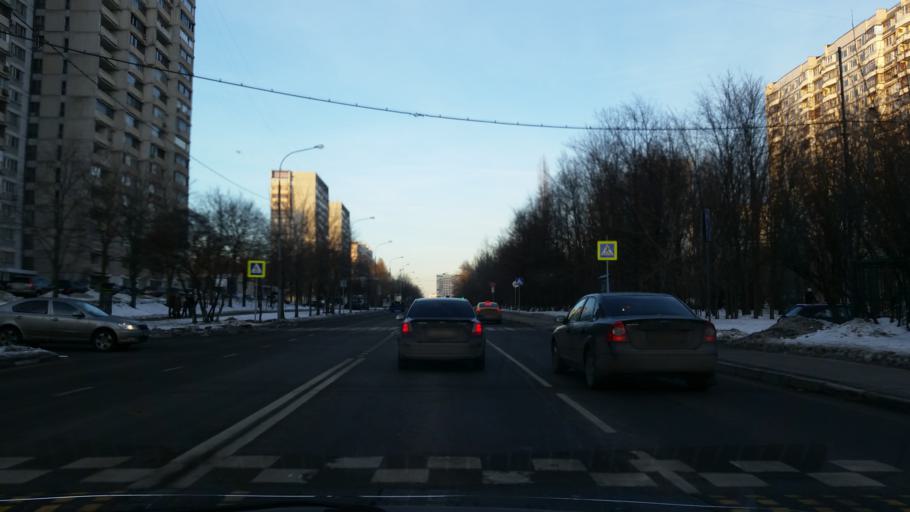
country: RU
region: Moscow
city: Nagornyy
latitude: 55.6263
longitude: 37.6107
